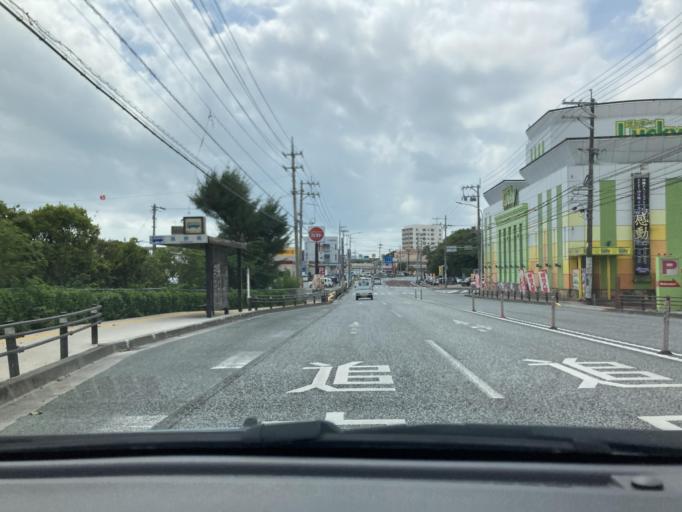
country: JP
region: Okinawa
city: Okinawa
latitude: 26.3205
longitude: 127.8216
